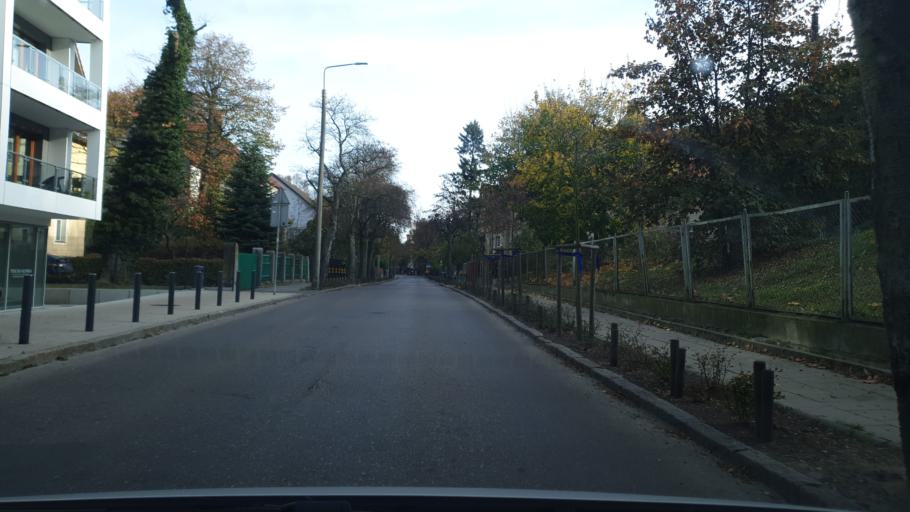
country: PL
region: Pomeranian Voivodeship
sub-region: Gdansk
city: Gdansk
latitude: 54.3770
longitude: 18.6009
